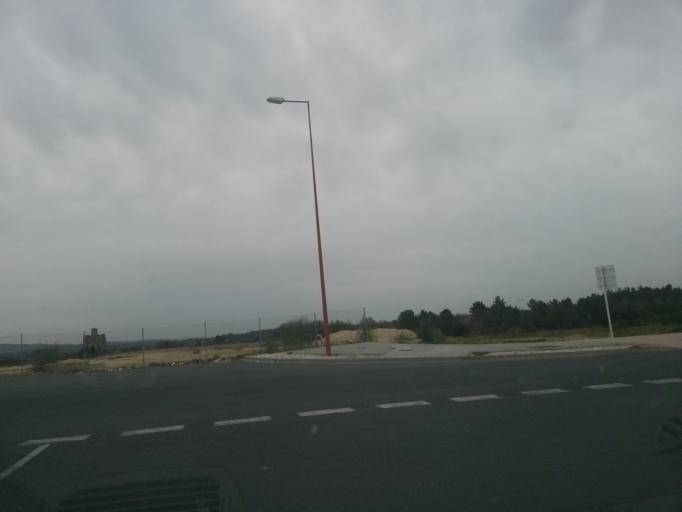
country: ES
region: Galicia
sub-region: Provincia de Lugo
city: Lugo
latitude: 43.0419
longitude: -7.5498
